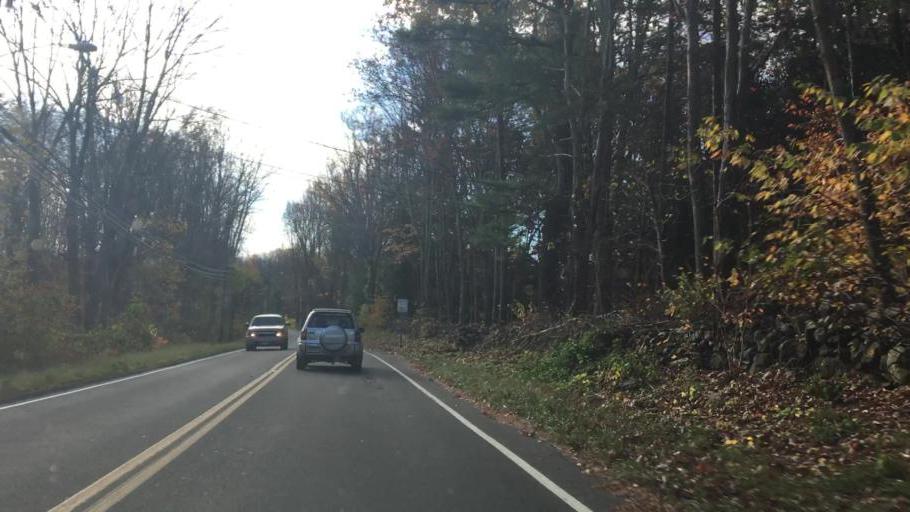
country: US
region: Connecticut
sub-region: New Haven County
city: Seymour
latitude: 41.3756
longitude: -73.1251
